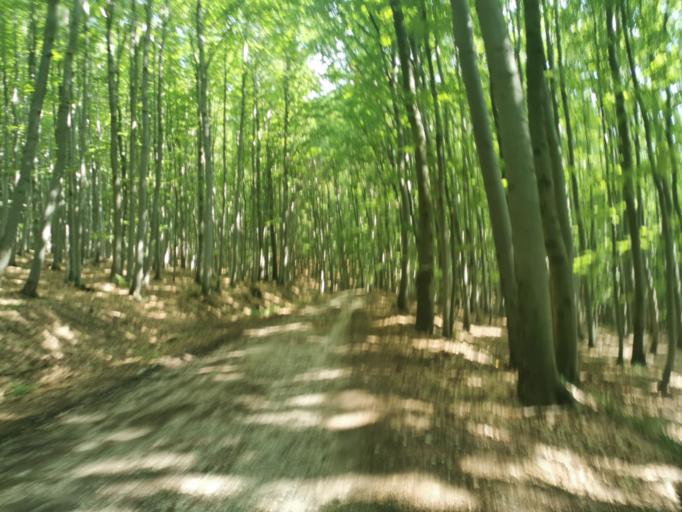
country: SK
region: Trenciansky
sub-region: Okres Myjava
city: Myjava
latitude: 48.8174
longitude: 17.5677
